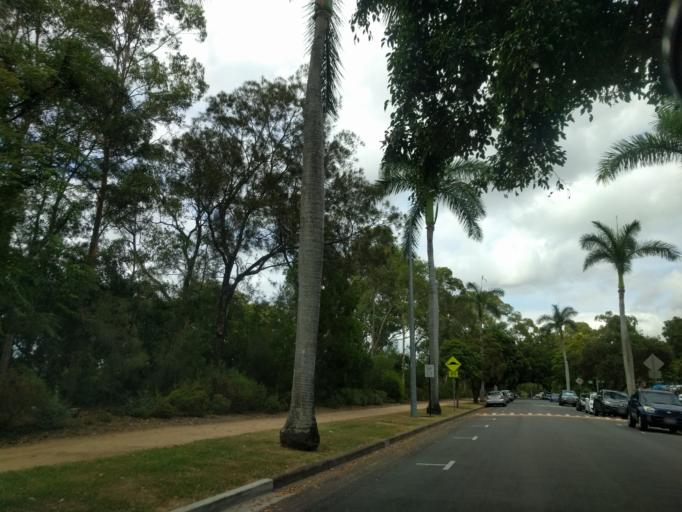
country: AU
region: Queensland
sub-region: Brisbane
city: Yeronga
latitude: -27.5021
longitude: 153.0165
